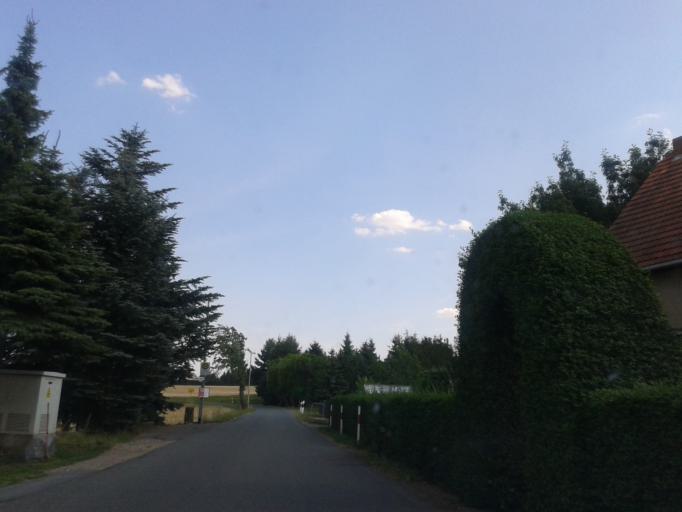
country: DE
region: Saxony
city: Niederschona
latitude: 50.9823
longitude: 13.4374
